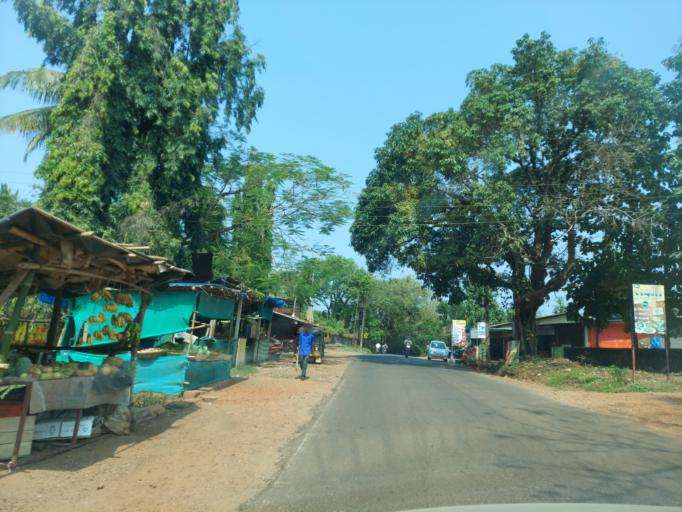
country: IN
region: Maharashtra
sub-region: Sindhudurg
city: Kudal
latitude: 15.9995
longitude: 73.6856
